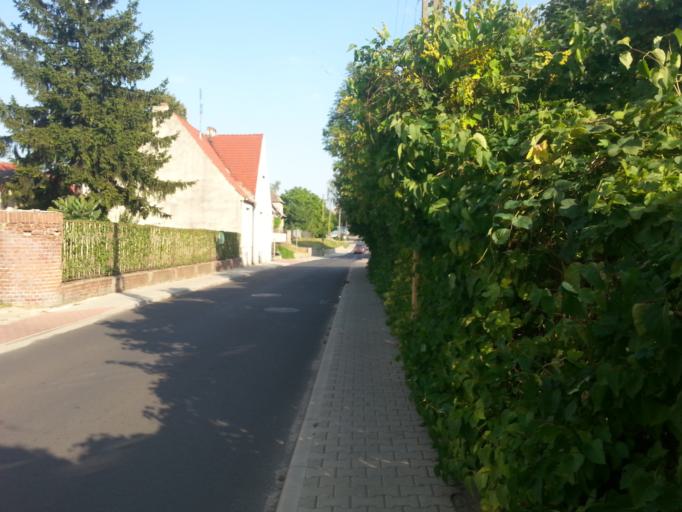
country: PL
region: Lower Silesian Voivodeship
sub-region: Powiat olesnicki
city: Twardogora
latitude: 51.3677
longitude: 17.4683
